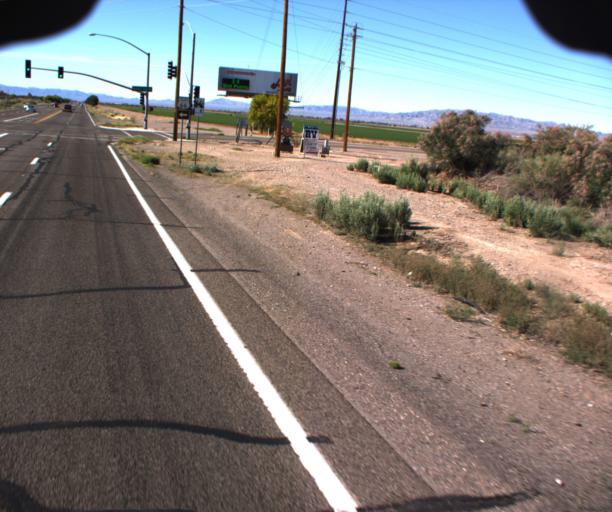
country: US
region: Arizona
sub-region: Mohave County
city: Mohave Valley
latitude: 34.9685
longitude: -114.5980
